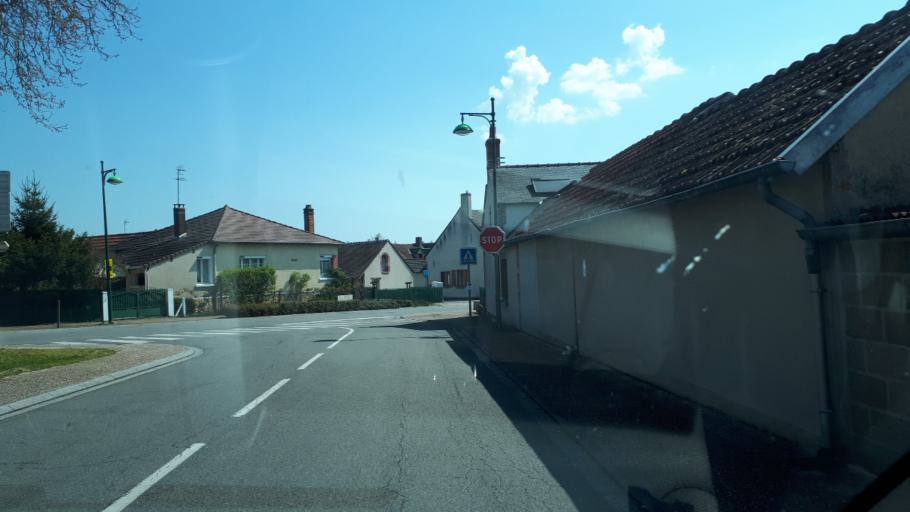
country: FR
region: Centre
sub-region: Departement du Cher
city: Neuvy-sur-Barangeon
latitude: 47.3159
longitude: 2.2525
